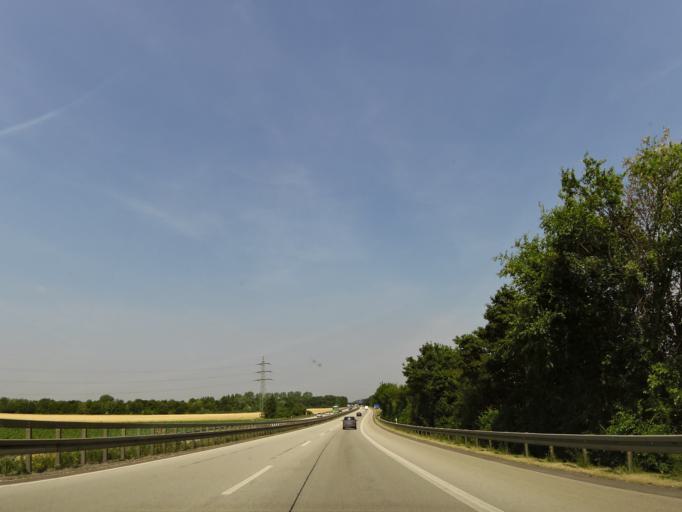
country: DE
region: North Rhine-Westphalia
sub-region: Regierungsbezirk Koln
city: Erftstadt
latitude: 50.8186
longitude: 6.7830
